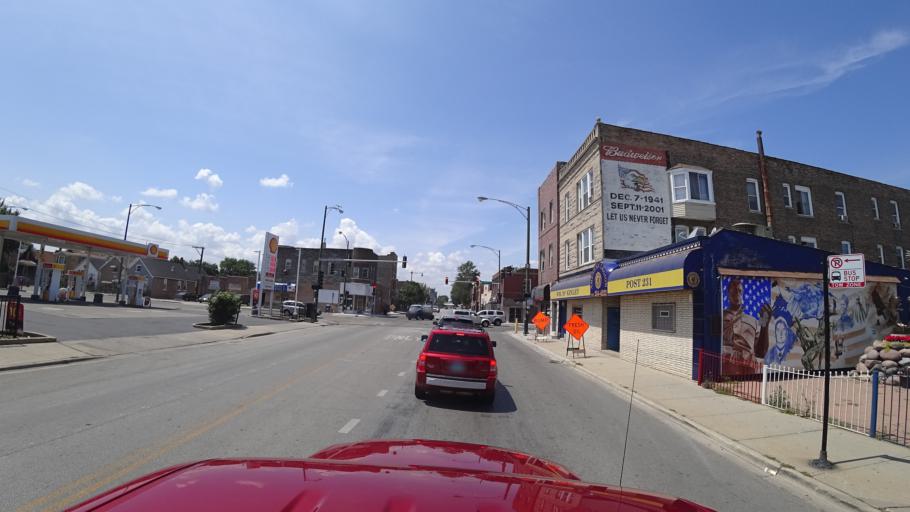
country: US
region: Illinois
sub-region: Cook County
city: Chicago
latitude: 41.8304
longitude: -87.6747
